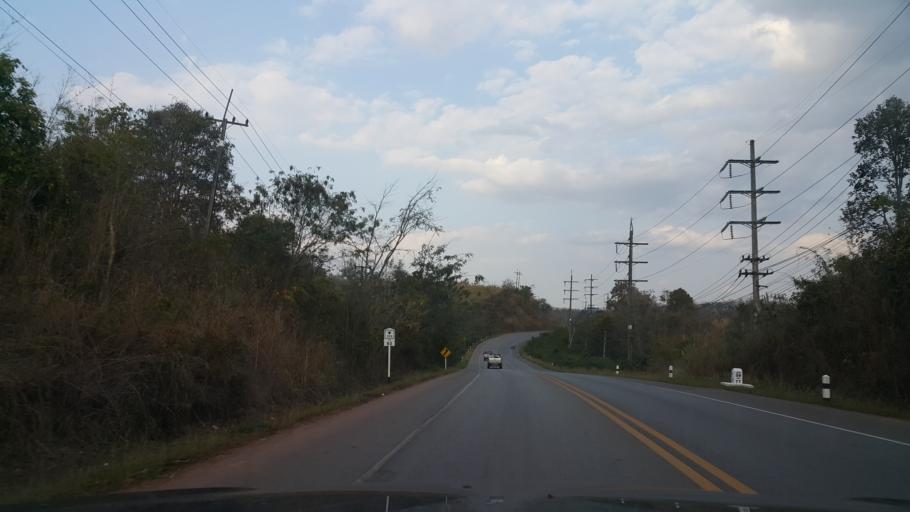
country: TH
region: Loei
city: Dan Sai
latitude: 17.3206
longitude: 101.2162
